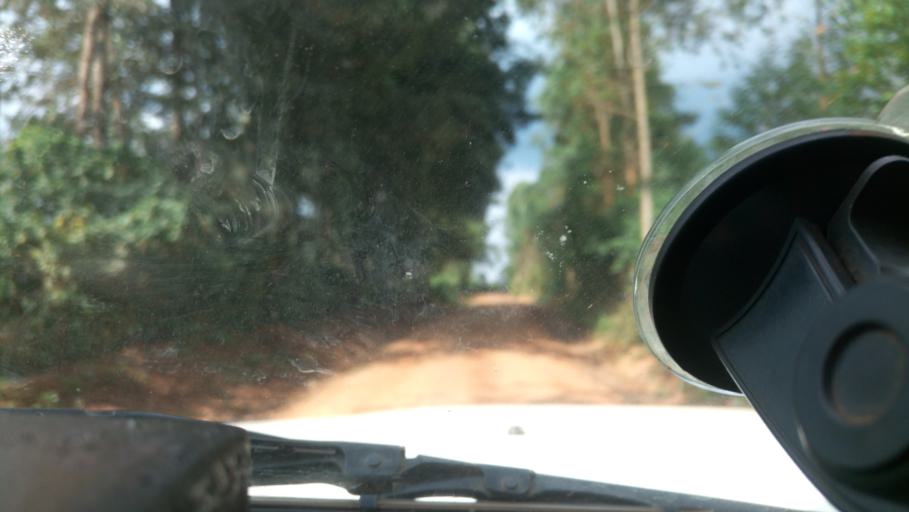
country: KE
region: Kericho
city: Sotik
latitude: -0.5898
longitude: 35.0798
